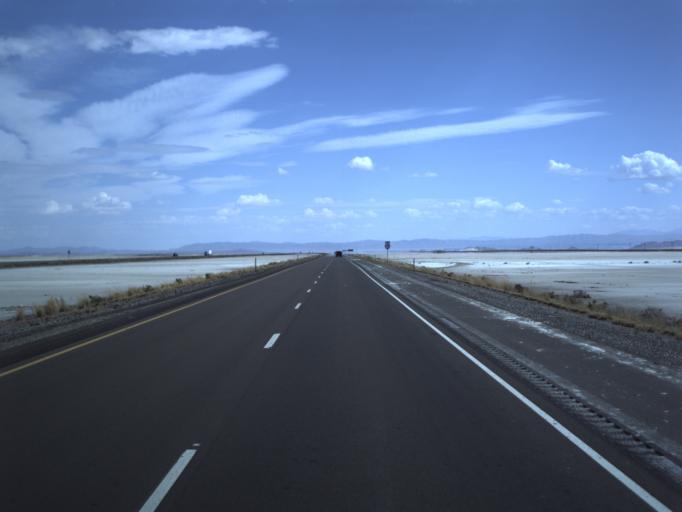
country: US
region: Utah
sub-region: Tooele County
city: Wendover
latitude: 40.7301
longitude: -113.4675
